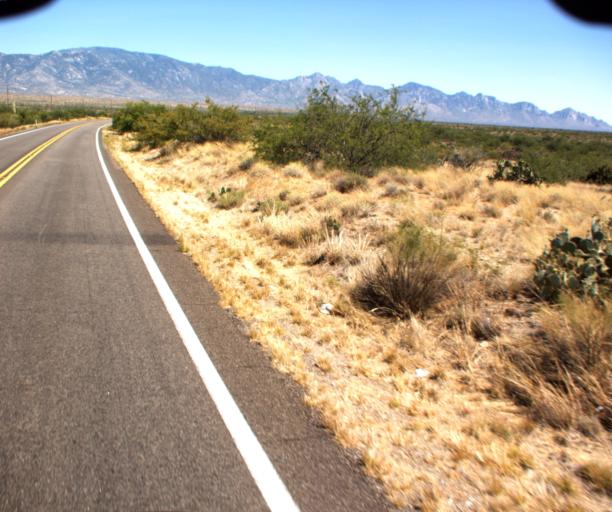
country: US
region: Arizona
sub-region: Pima County
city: Catalina
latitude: 32.5810
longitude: -110.9531
